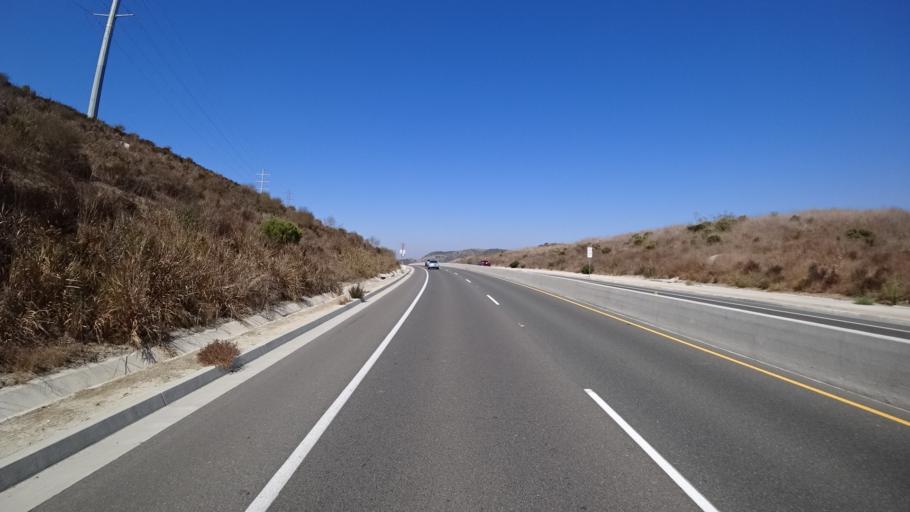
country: US
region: California
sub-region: Orange County
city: San Clemente
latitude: 33.4780
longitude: -117.6084
